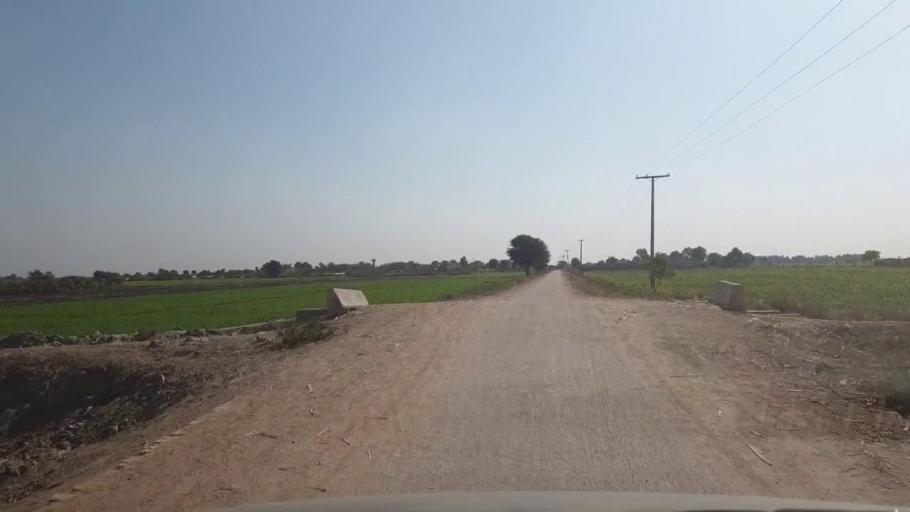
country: PK
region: Sindh
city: Chambar
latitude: 25.3234
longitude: 68.8656
